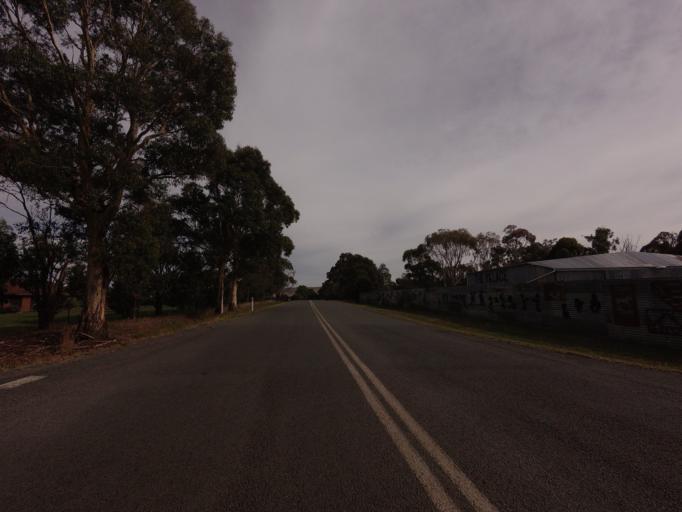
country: AU
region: Tasmania
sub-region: Brighton
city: Bridgewater
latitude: -42.3081
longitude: 147.3652
